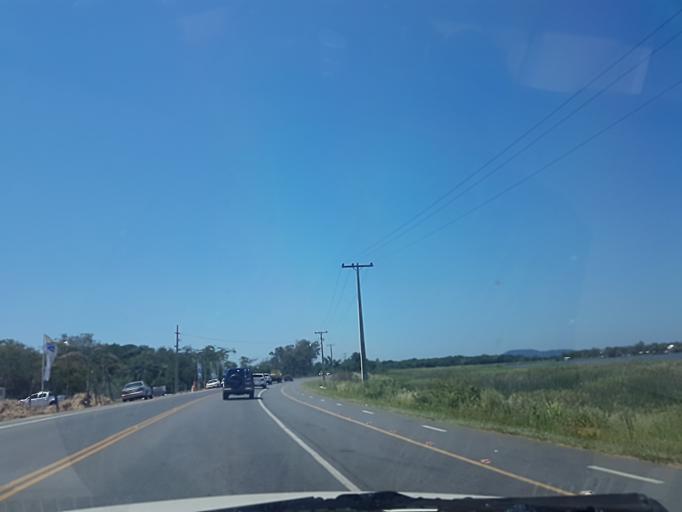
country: PY
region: Cordillera
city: San Bernardino
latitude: -25.2741
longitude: -57.3177
